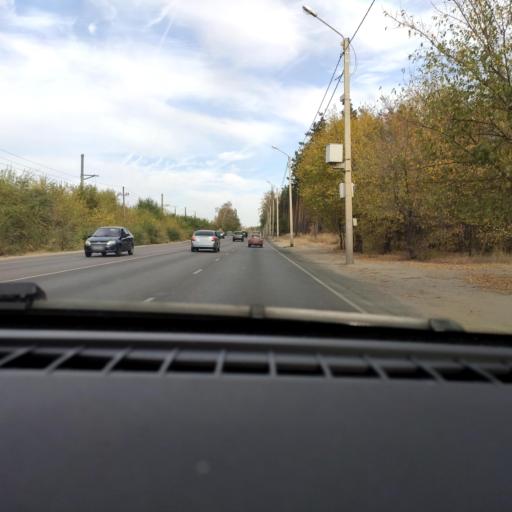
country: RU
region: Voronezj
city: Voronezh
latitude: 51.6749
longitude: 39.2728
